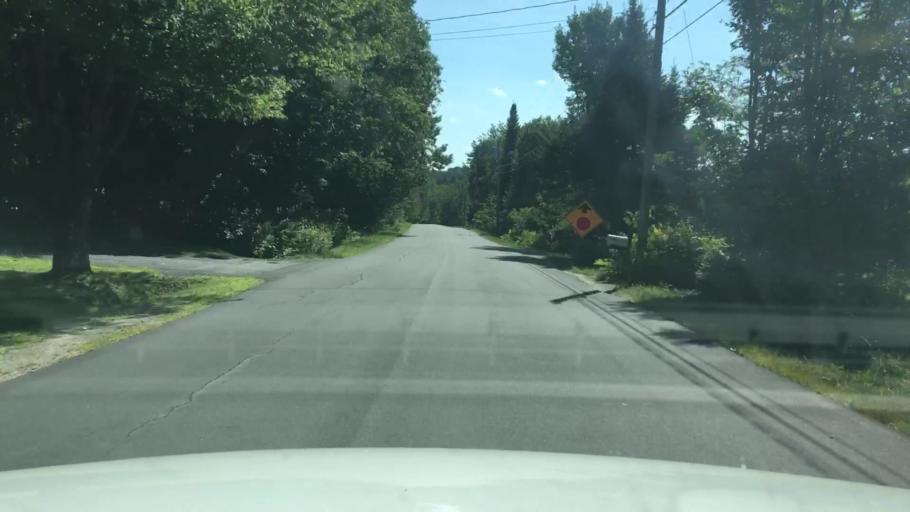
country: US
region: Maine
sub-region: Kennebec County
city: Monmouth
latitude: 44.2586
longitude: -70.0562
